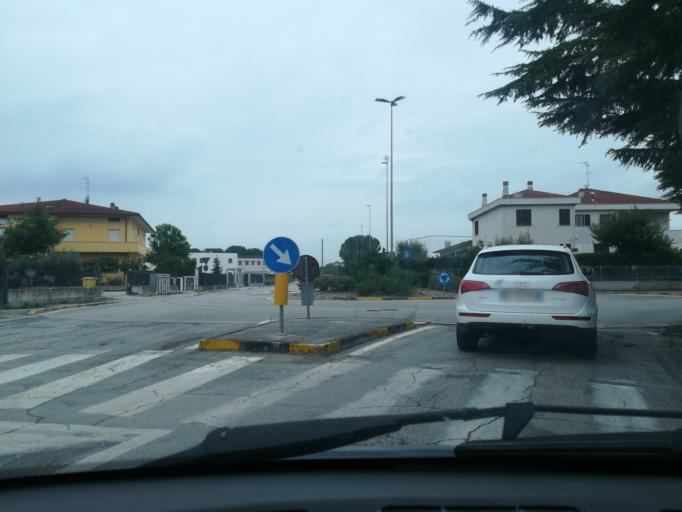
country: IT
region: The Marches
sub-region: Provincia di Macerata
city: Piediripa
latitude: 43.2764
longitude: 13.4958
